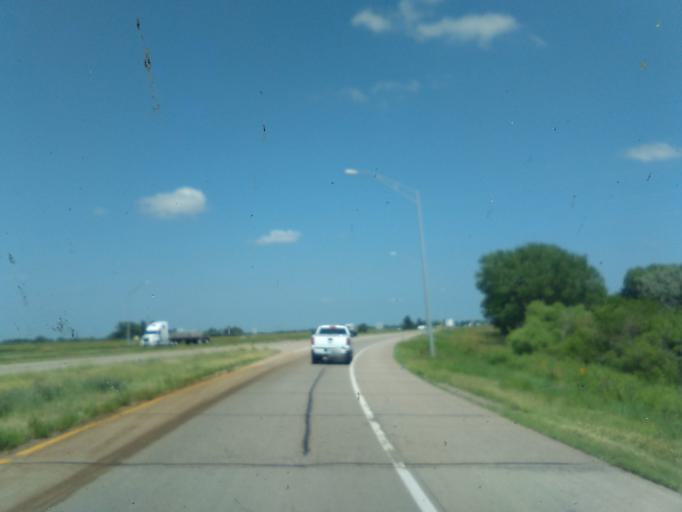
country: US
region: Nebraska
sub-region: Phelps County
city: Holdrege
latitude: 40.6898
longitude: -99.3765
